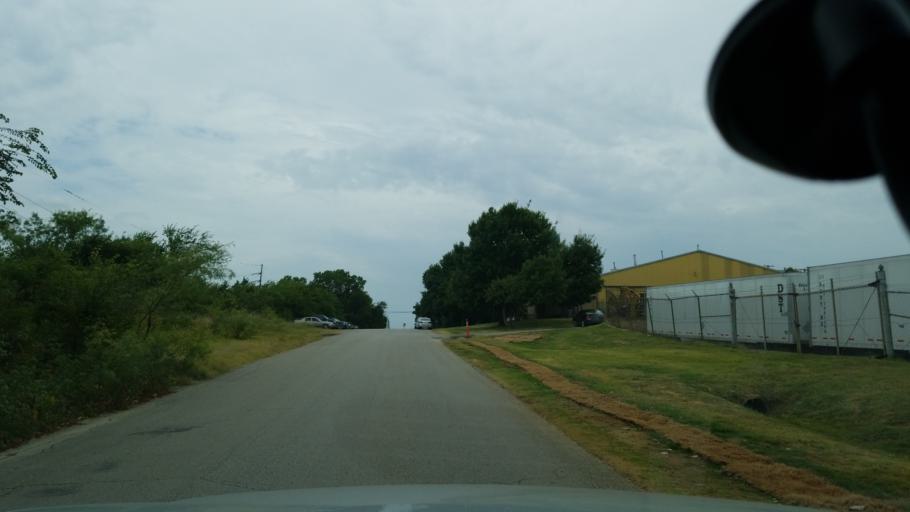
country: US
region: Texas
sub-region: Dallas County
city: Grand Prairie
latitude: 32.7349
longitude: -96.9834
